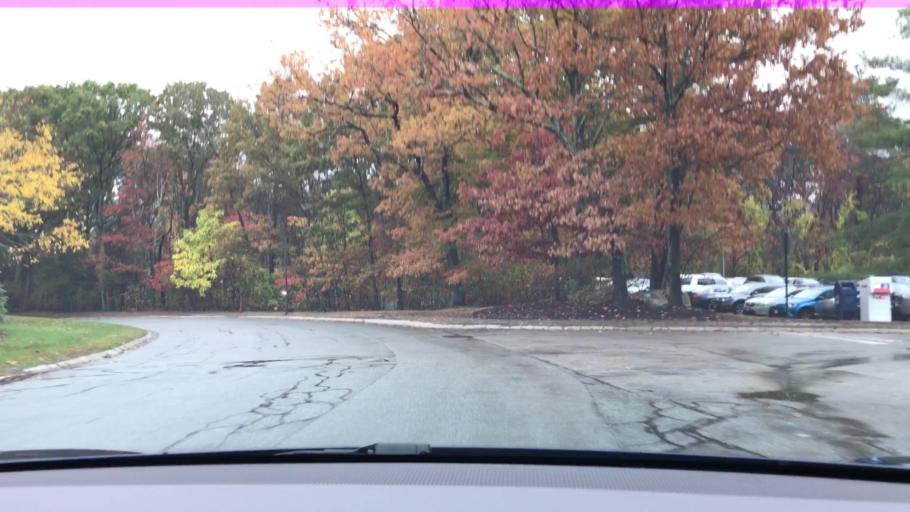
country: US
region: Massachusetts
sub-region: Middlesex County
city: Billerica
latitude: 42.5313
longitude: -71.2814
